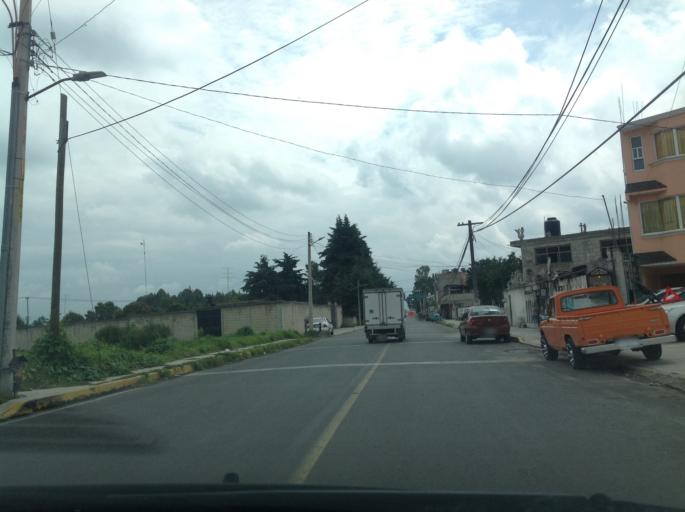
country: MX
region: Morelos
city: Tenango de Arista
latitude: 19.1040
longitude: -99.5821
